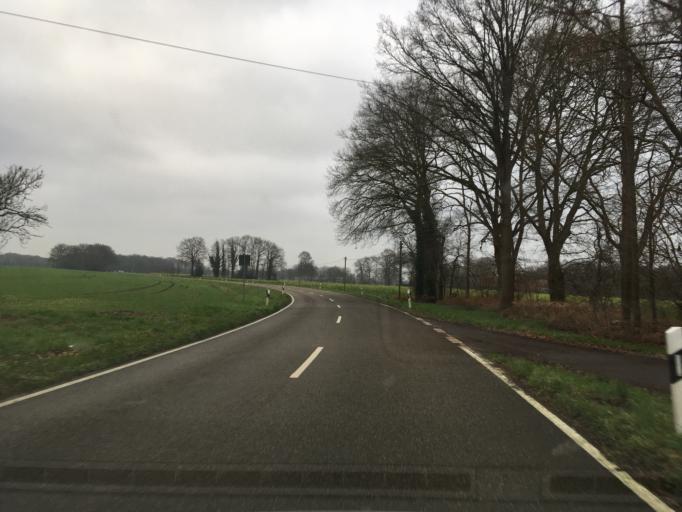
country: DE
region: North Rhine-Westphalia
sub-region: Regierungsbezirk Munster
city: Gronau
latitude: 52.1763
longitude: 7.0757
